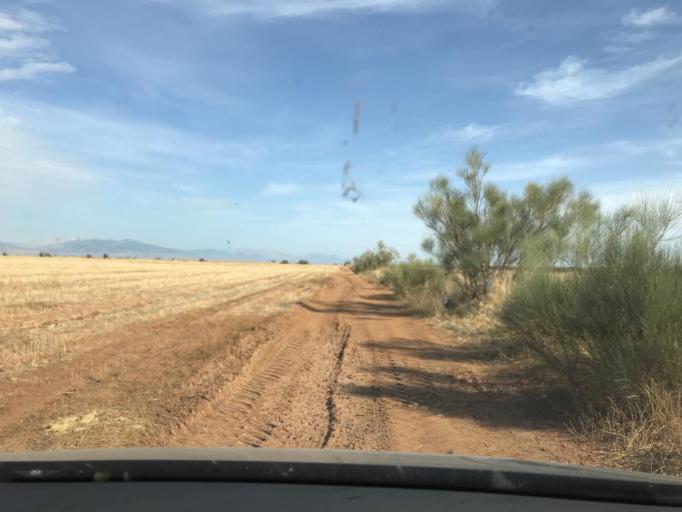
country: ES
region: Andalusia
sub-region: Provincia de Granada
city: Villanueva de las Torres
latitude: 37.4699
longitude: -3.0604
